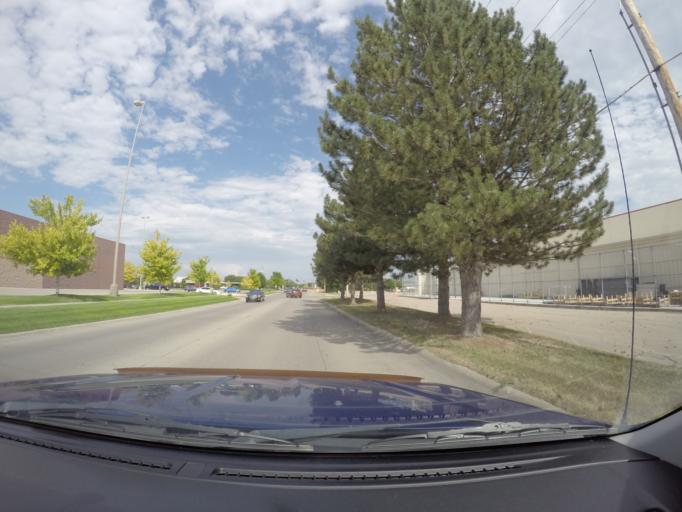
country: US
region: Nebraska
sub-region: Buffalo County
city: Kearney
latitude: 40.7213
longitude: -99.0864
